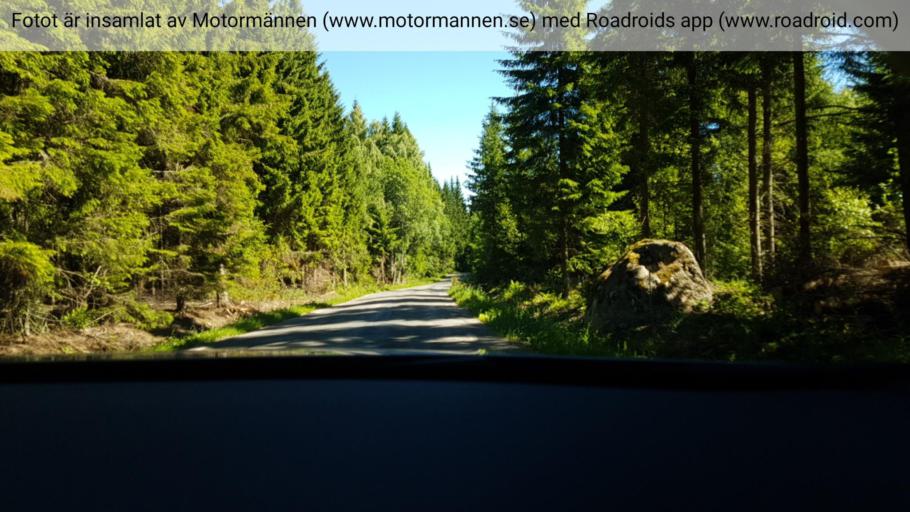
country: SE
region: Vaestra Goetaland
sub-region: Falkopings Kommun
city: Akarp
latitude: 58.1891
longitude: 13.7887
